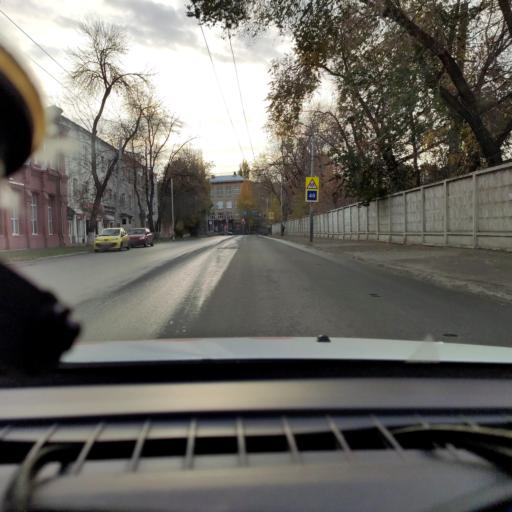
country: RU
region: Samara
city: Samara
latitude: 53.1976
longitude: 50.1274
